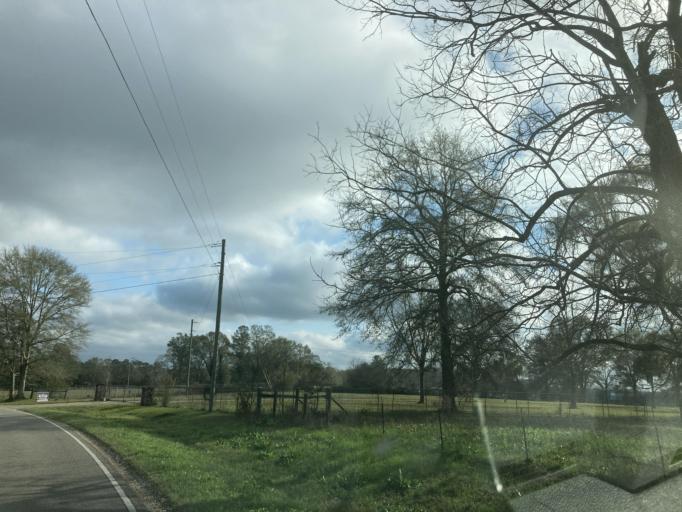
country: US
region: Mississippi
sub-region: Stone County
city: Wiggins
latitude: 30.8116
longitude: -89.1014
